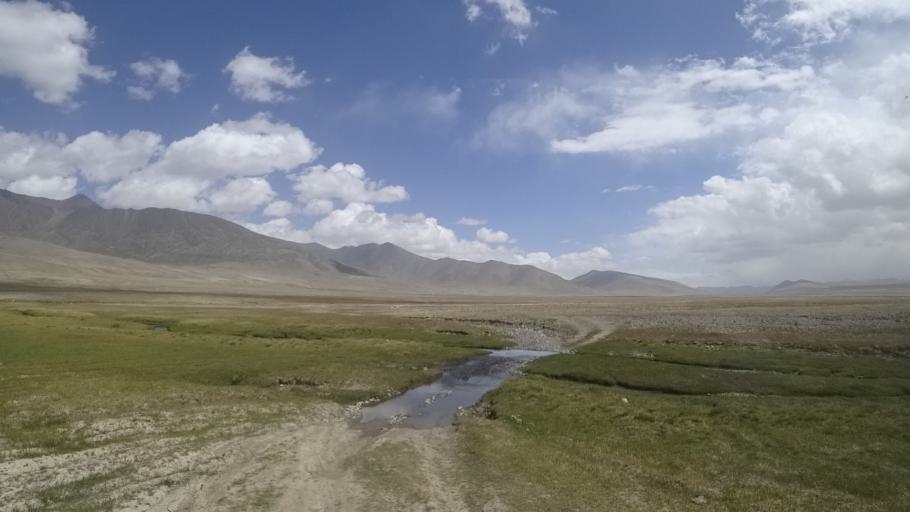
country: TJ
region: Gorno-Badakhshan
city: Murghob
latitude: 37.4765
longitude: 73.9751
